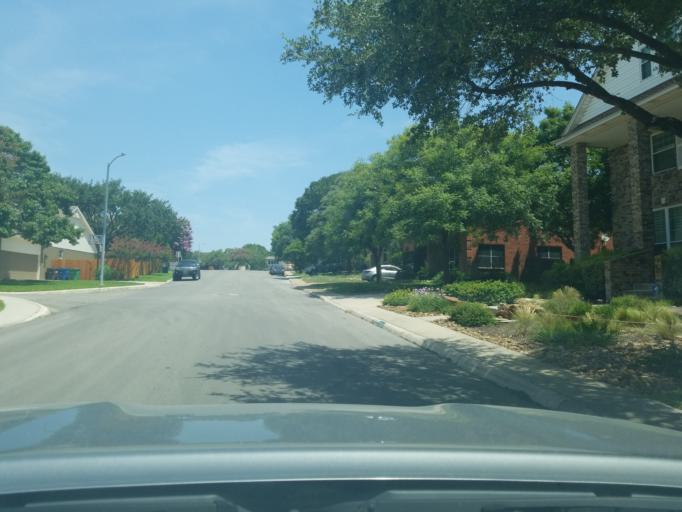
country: US
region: Texas
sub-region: Bexar County
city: Hollywood Park
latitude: 29.6437
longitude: -98.4939
